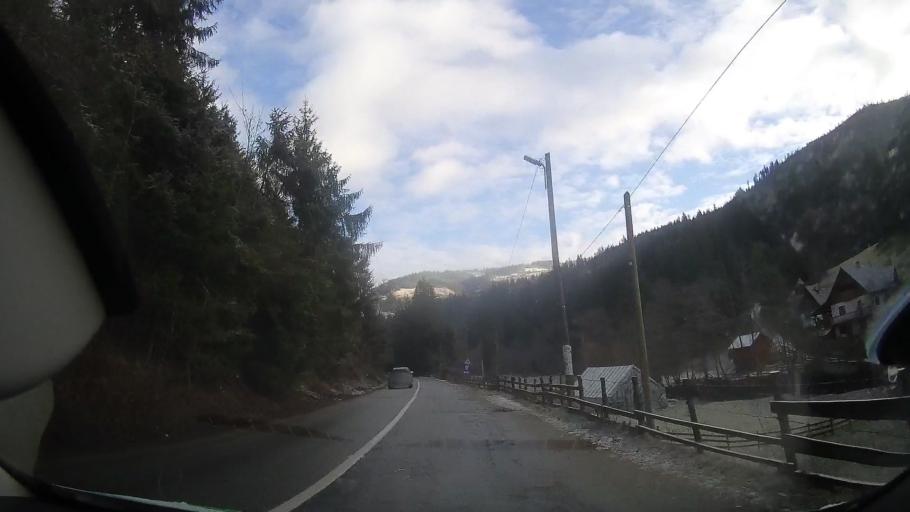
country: RO
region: Alba
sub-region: Comuna Albac
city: Albac
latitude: 46.4506
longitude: 22.9692
